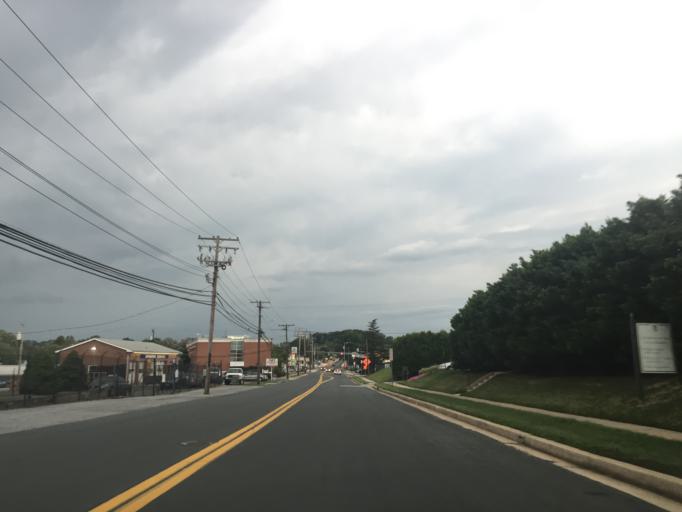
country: US
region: Maryland
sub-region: Baltimore County
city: Parkville
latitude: 39.3885
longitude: -76.5443
